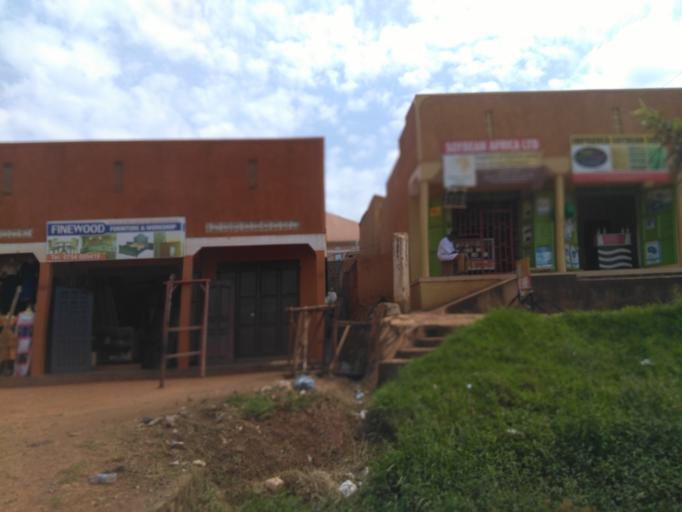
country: UG
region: Central Region
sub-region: Wakiso District
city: Kireka
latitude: 0.4545
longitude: 32.6065
